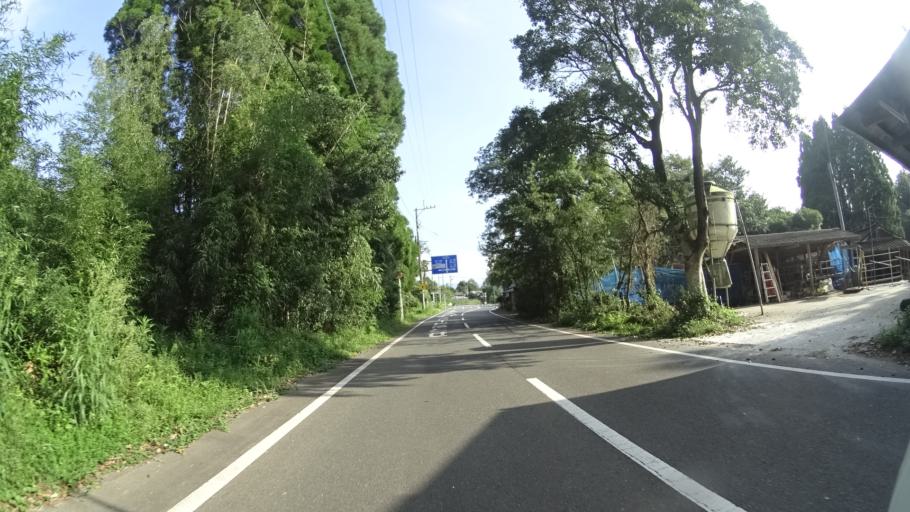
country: JP
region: Kagoshima
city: Okuchi-shinohara
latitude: 32.0153
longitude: 130.5773
